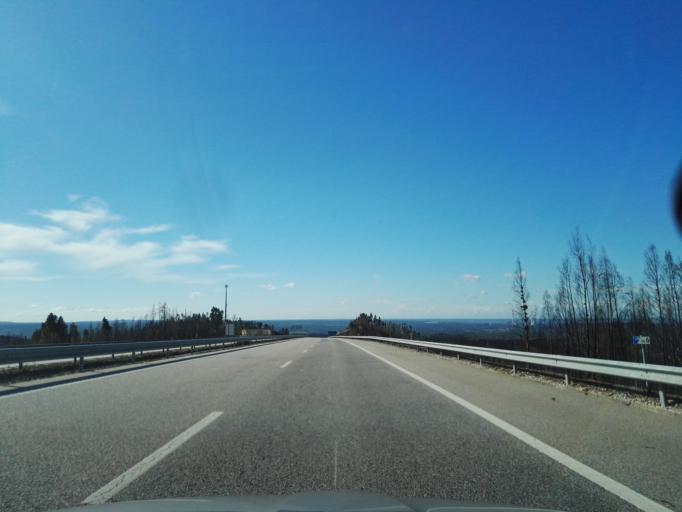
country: PT
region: Santarem
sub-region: Macao
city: Macao
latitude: 39.5088
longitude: -8.0197
